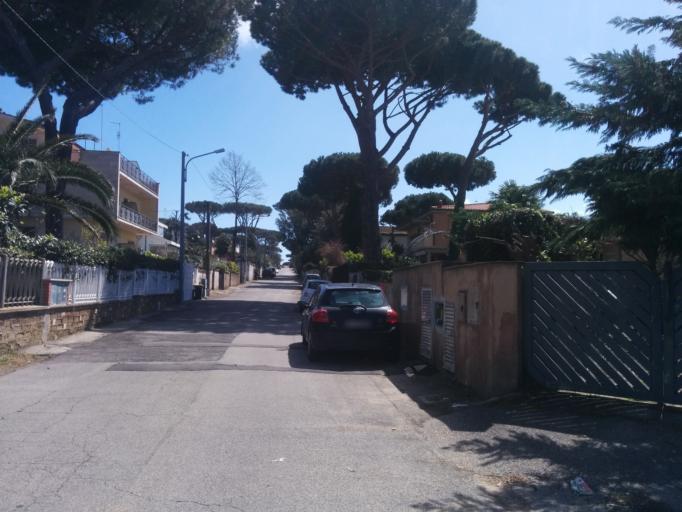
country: IT
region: Latium
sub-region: Citta metropolitana di Roma Capitale
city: Lavinio
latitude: 41.5010
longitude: 12.5955
